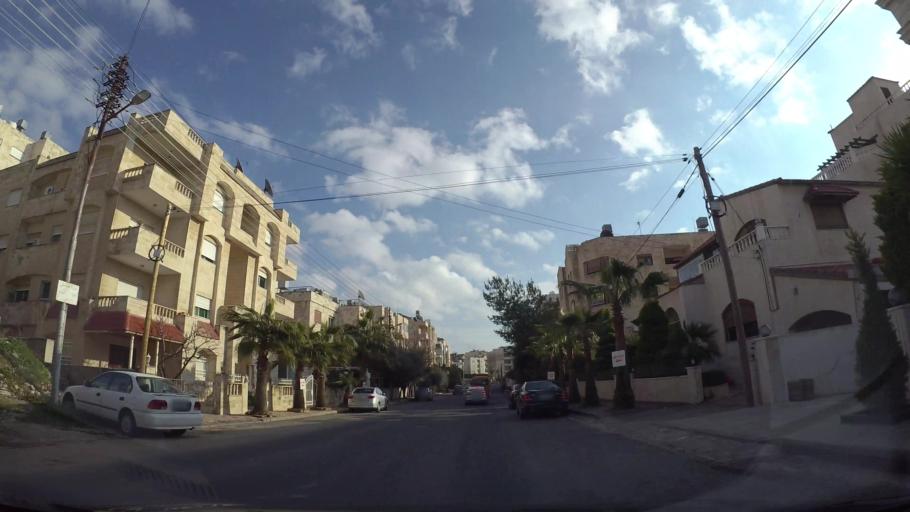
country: JO
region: Amman
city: Al Jubayhah
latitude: 31.9814
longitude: 35.8756
